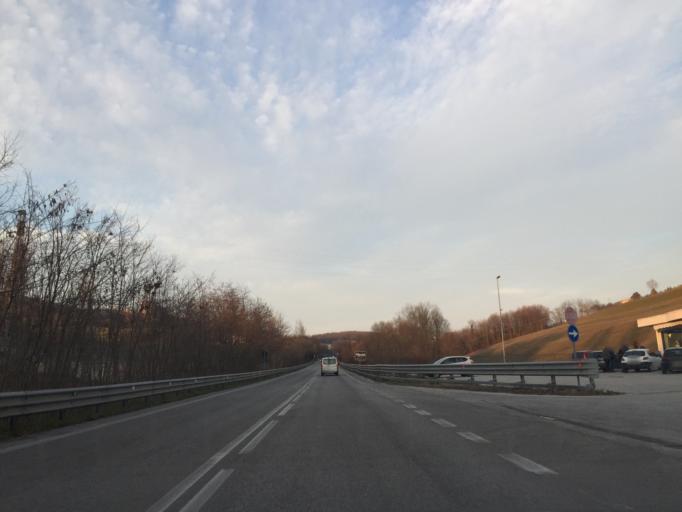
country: IT
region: Molise
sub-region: Provincia di Campobasso
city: Mimosa-Poggio Verde-Nuova Comunita
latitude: 41.5385
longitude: 14.6175
